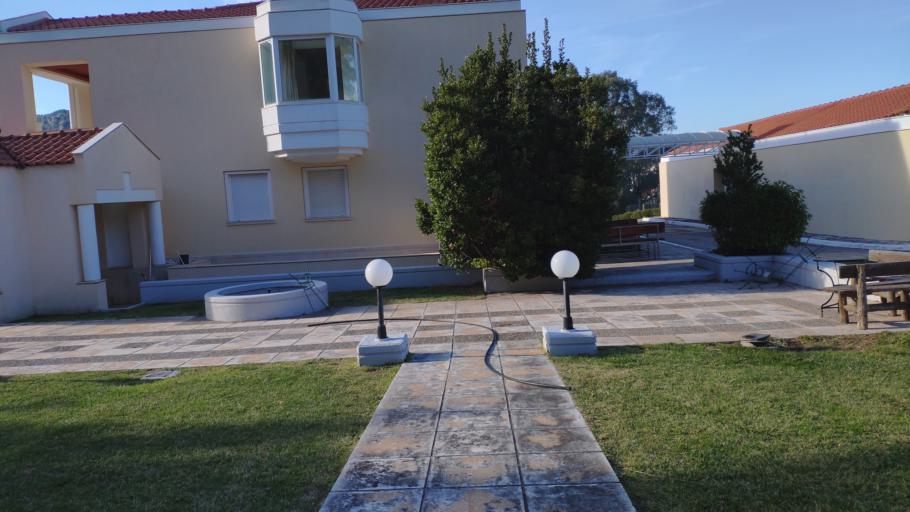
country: GR
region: Peloponnese
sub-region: Nomos Korinthias
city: Perachora
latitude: 38.0456
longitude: 23.0326
